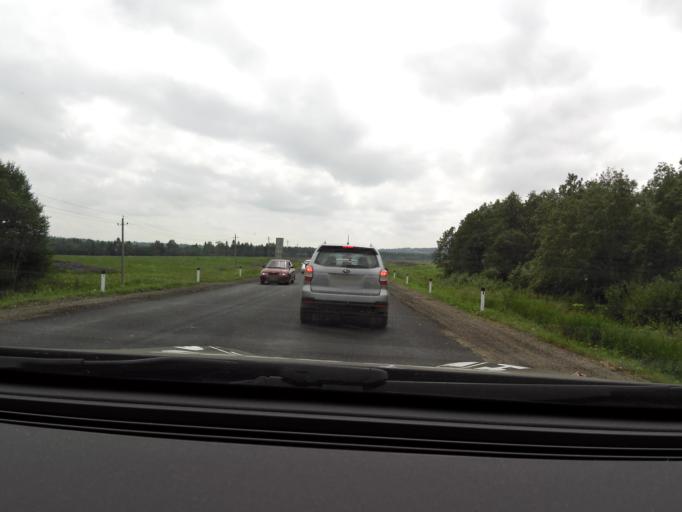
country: RU
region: Perm
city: Zvezdnyy
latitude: 57.7791
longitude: 56.3459
